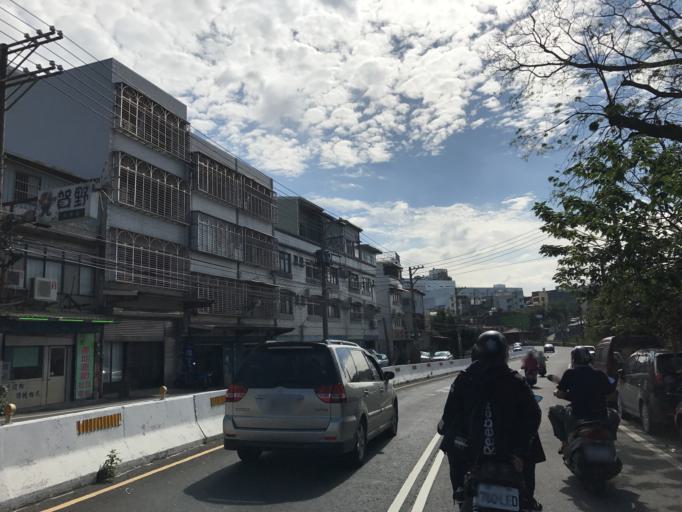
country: TW
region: Taiwan
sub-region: Hsinchu
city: Zhubei
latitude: 24.7620
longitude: 121.0612
